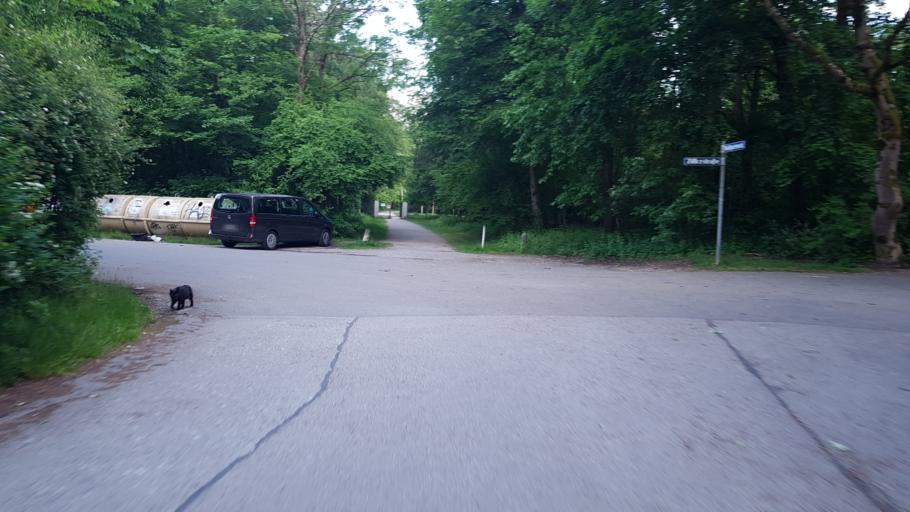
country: DE
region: Bavaria
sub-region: Upper Bavaria
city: Neuried
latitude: 48.1031
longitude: 11.4829
